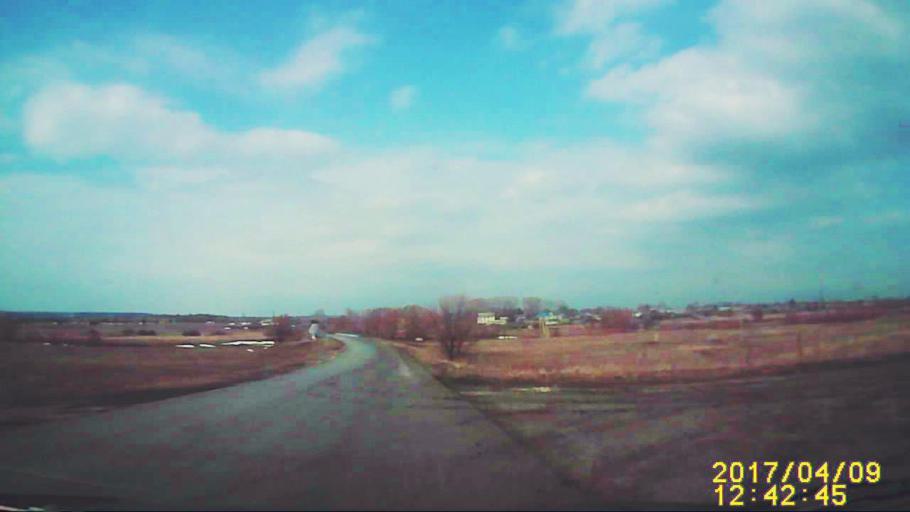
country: RU
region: Ulyanovsk
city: Ignatovka
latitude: 54.0045
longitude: 47.9247
